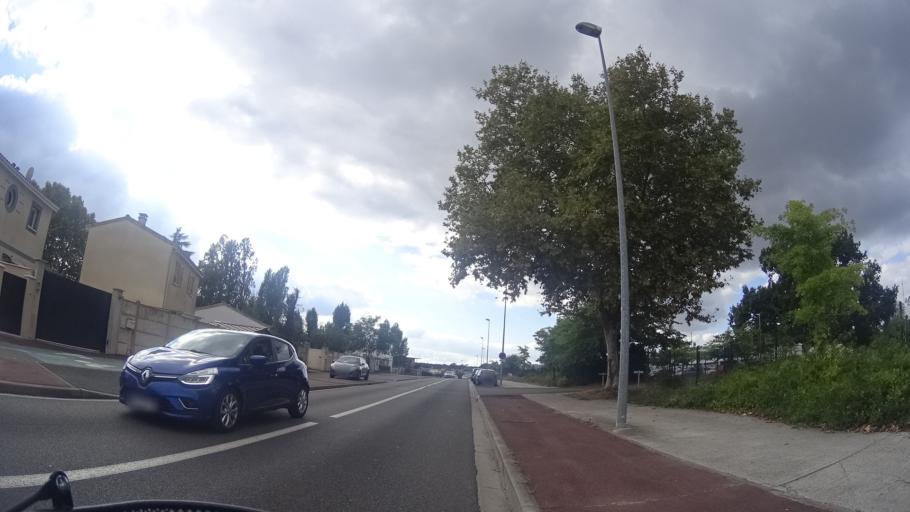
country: FR
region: Aquitaine
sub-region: Departement de la Gironde
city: Talence
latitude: 44.7858
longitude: -0.5804
